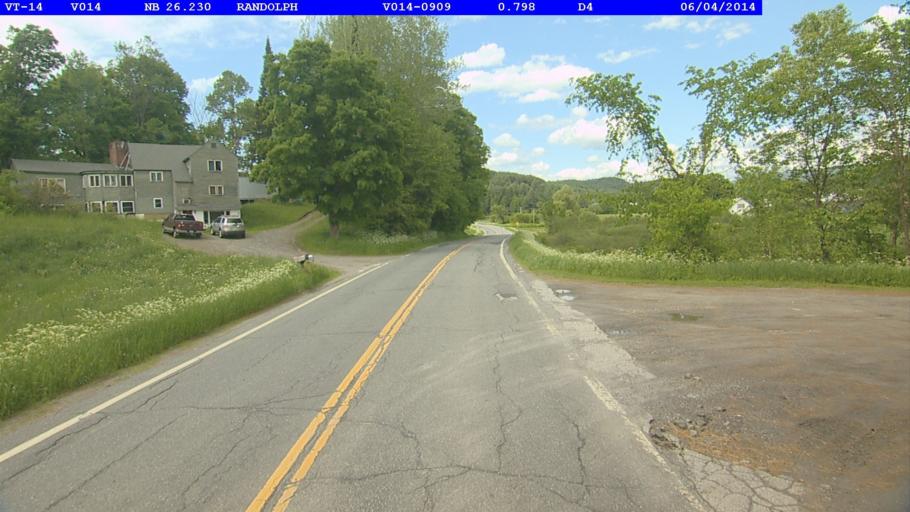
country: US
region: Vermont
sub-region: Orange County
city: Randolph
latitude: 43.8873
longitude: -72.5809
